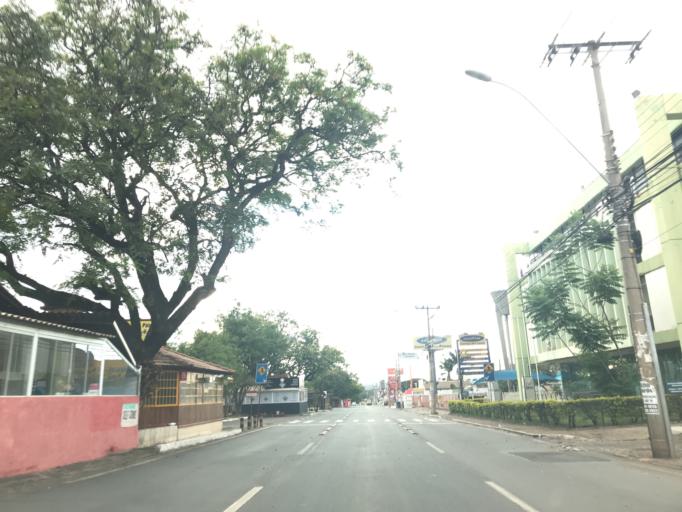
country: BR
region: Federal District
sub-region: Brasilia
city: Brasilia
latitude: -15.8057
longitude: -47.9617
